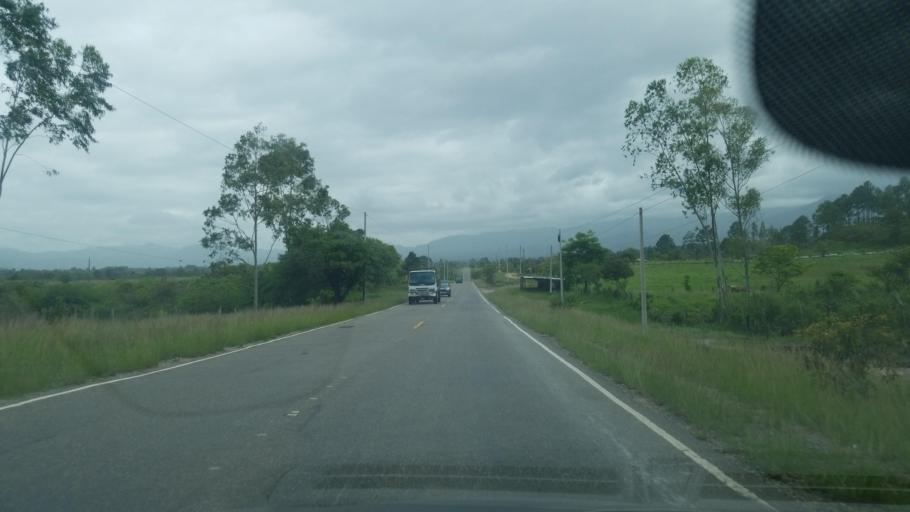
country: HN
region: Ocotepeque
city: Lucerna
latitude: 14.5393
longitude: -88.9467
